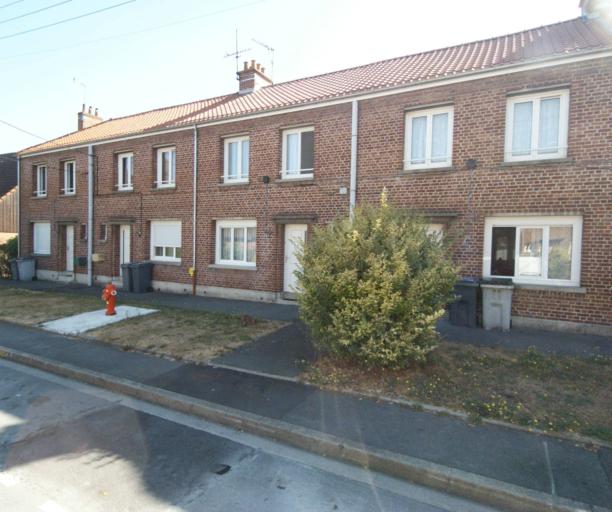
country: FR
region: Nord-Pas-de-Calais
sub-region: Departement du Nord
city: Wervicq-Sud
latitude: 50.7720
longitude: 3.0522
